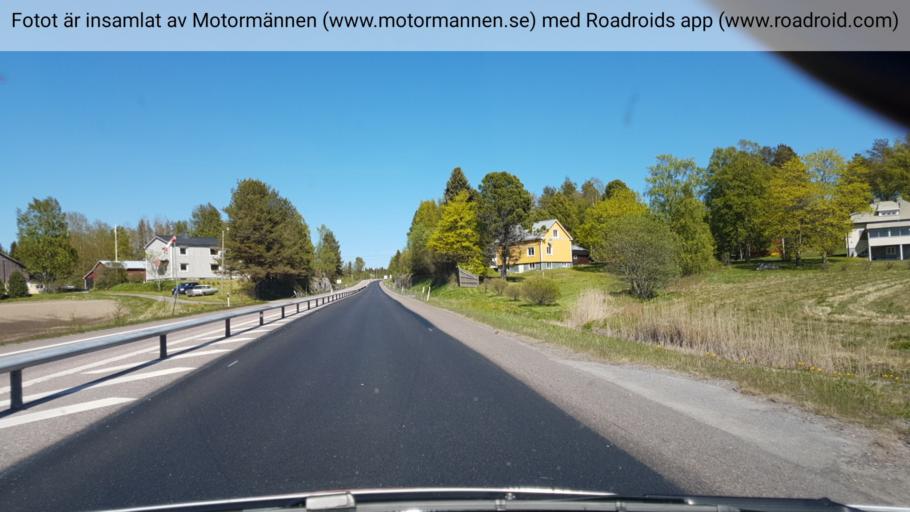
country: SE
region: Vaesternorrland
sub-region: OErnskoeldsviks Kommun
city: Husum
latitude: 63.3309
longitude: 19.0592
